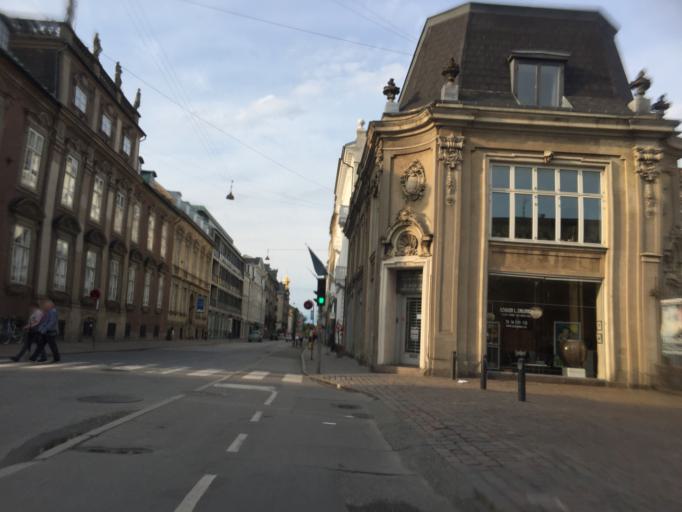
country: DK
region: Capital Region
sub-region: Kobenhavn
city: Christianshavn
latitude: 55.6829
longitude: 12.5892
